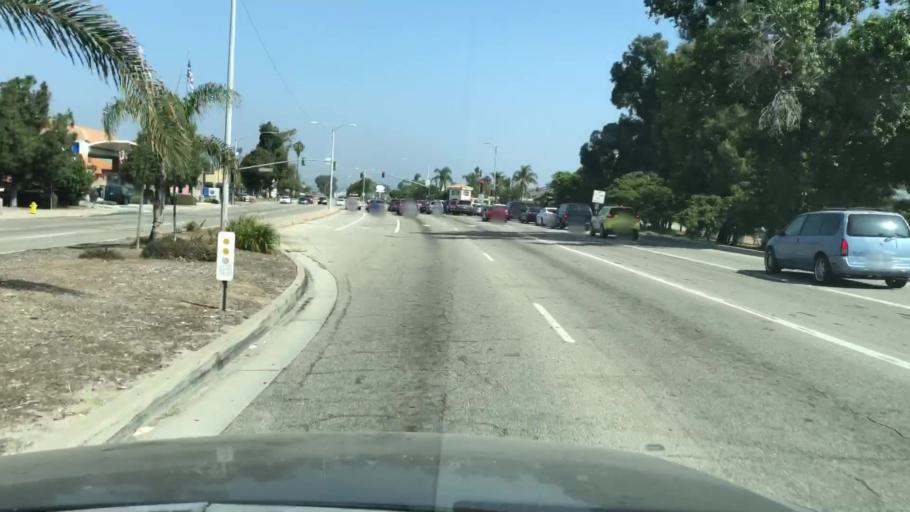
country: US
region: California
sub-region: Ventura County
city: El Rio
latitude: 34.2252
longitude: -119.1771
